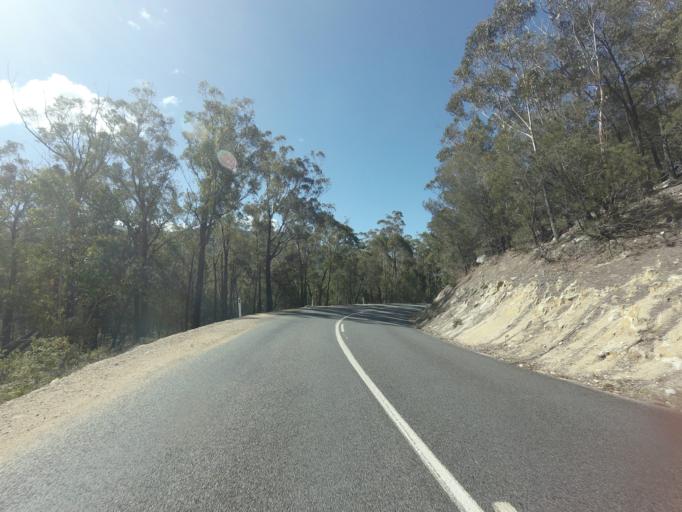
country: AU
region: Tasmania
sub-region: Break O'Day
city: St Helens
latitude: -41.6619
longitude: 148.2703
